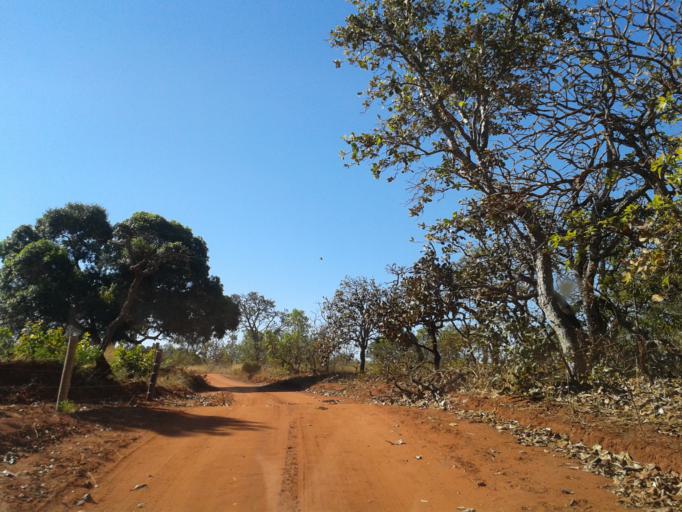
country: BR
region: Minas Gerais
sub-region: Ituiutaba
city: Ituiutaba
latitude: -19.0841
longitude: -49.3369
